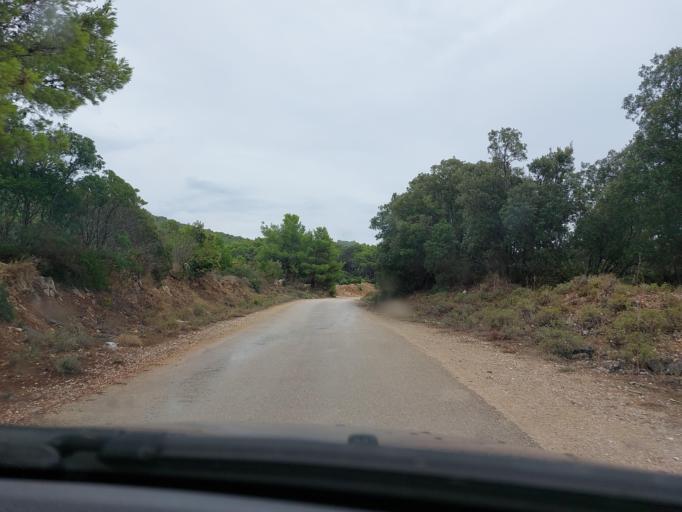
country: HR
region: Dubrovacko-Neretvanska
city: Smokvica
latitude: 42.7410
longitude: 16.8293
